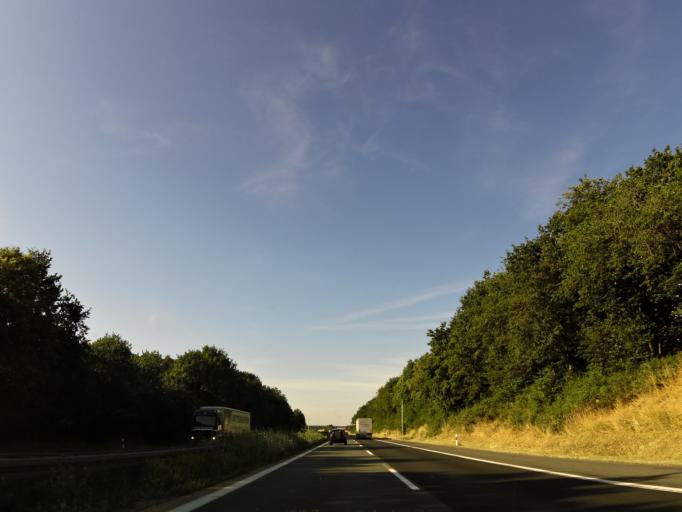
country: DE
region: Bavaria
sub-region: Regierungsbezirk Mittelfranken
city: Hessdorf
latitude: 49.5963
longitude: 10.9269
